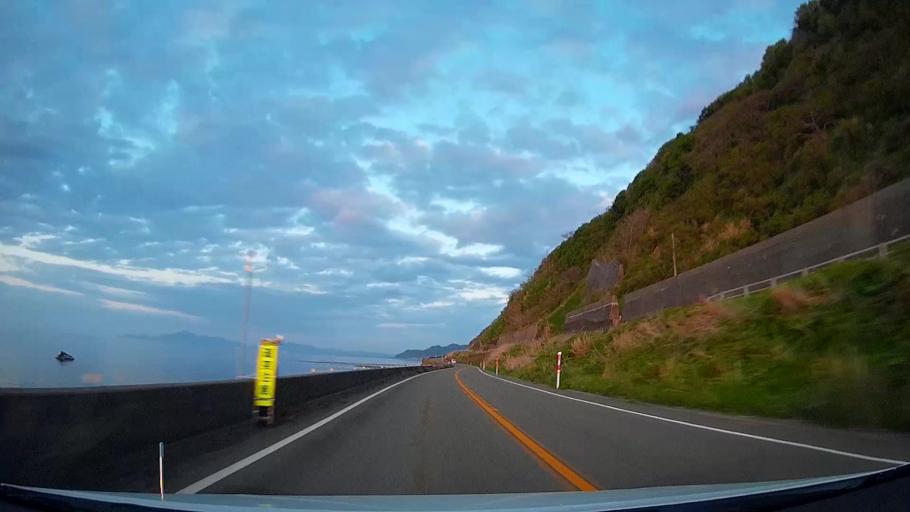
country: JP
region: Niigata
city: Joetsu
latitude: 37.1723
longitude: 138.1071
